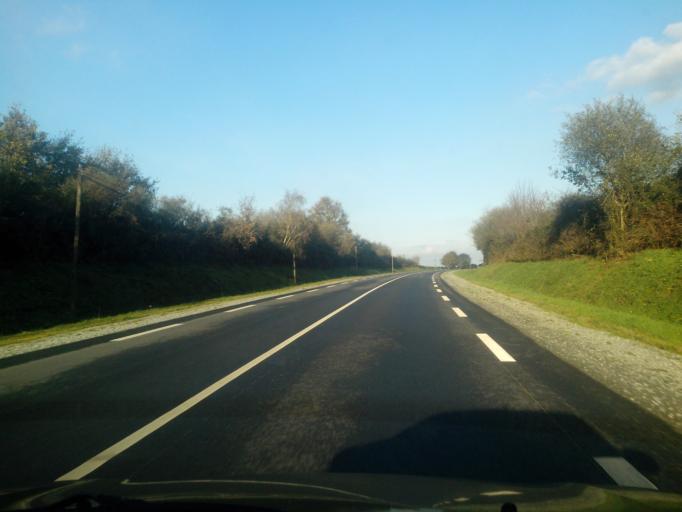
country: FR
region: Brittany
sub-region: Departement du Morbihan
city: Mauron
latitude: 48.0518
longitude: -2.3003
